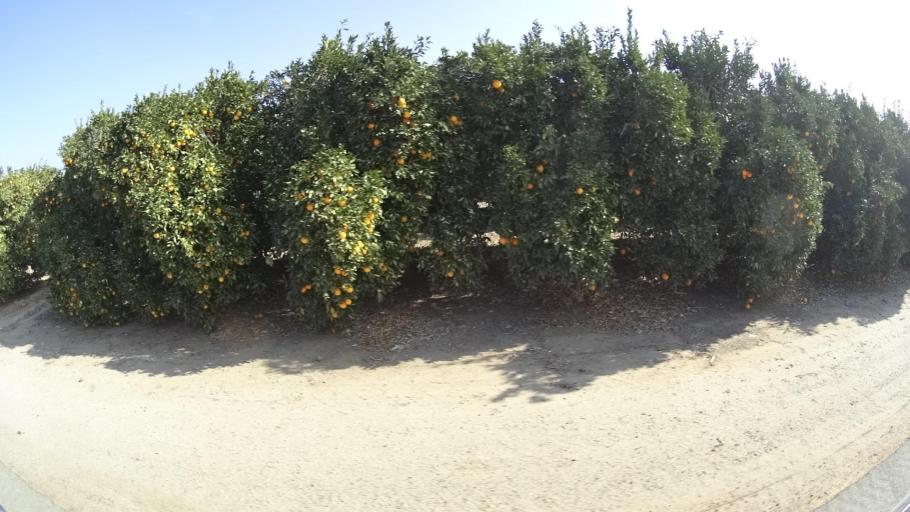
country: US
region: California
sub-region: Kern County
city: McFarland
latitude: 35.6142
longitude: -119.1865
